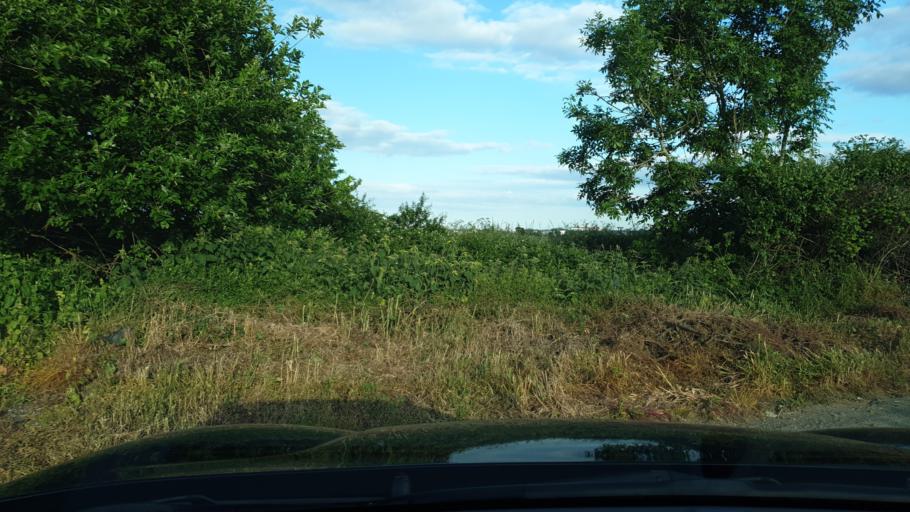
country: IE
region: Leinster
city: Hartstown
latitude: 53.4334
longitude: -6.4042
